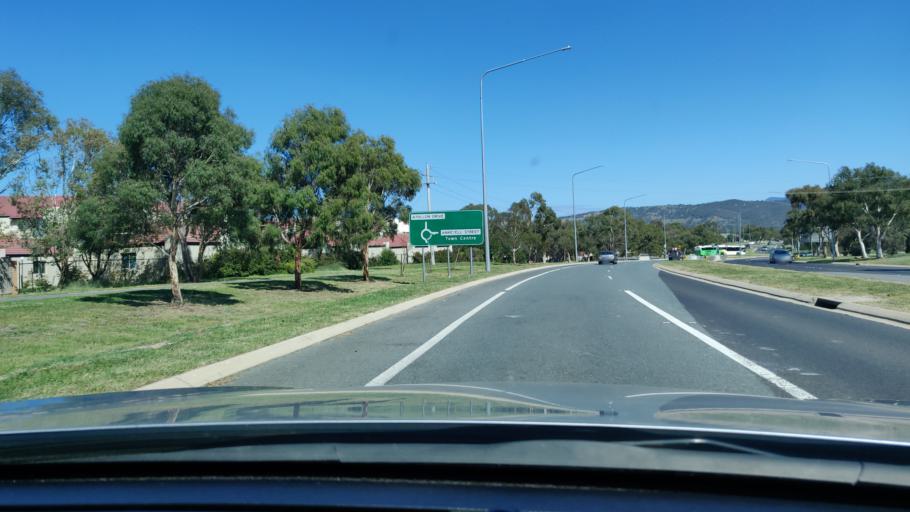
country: AU
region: Australian Capital Territory
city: Macarthur
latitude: -35.4244
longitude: 149.0768
